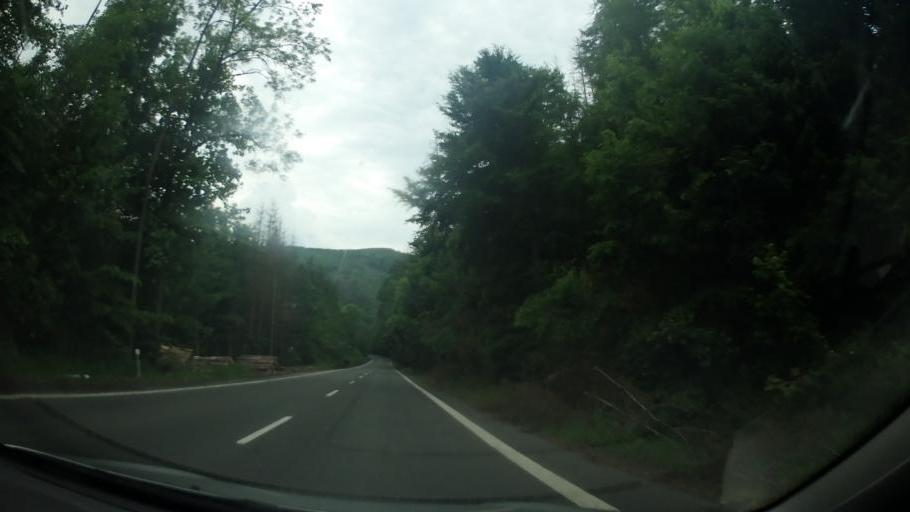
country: CZ
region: South Moravian
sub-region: Okres Brno-Venkov
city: Nedvedice
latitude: 49.4927
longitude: 16.3798
